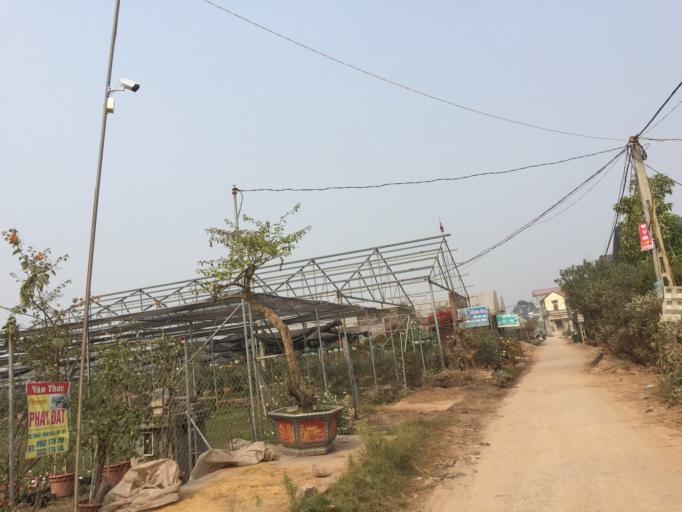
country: VN
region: Hung Yen
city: Van Giang
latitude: 20.9678
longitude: 105.9149
